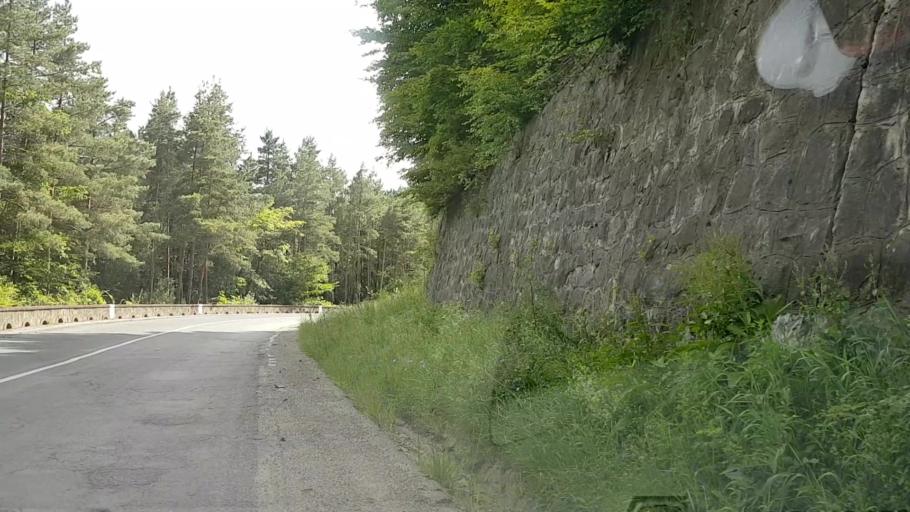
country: RO
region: Neamt
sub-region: Comuna Bicaz
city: Dodeni
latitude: 46.9386
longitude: 26.0994
